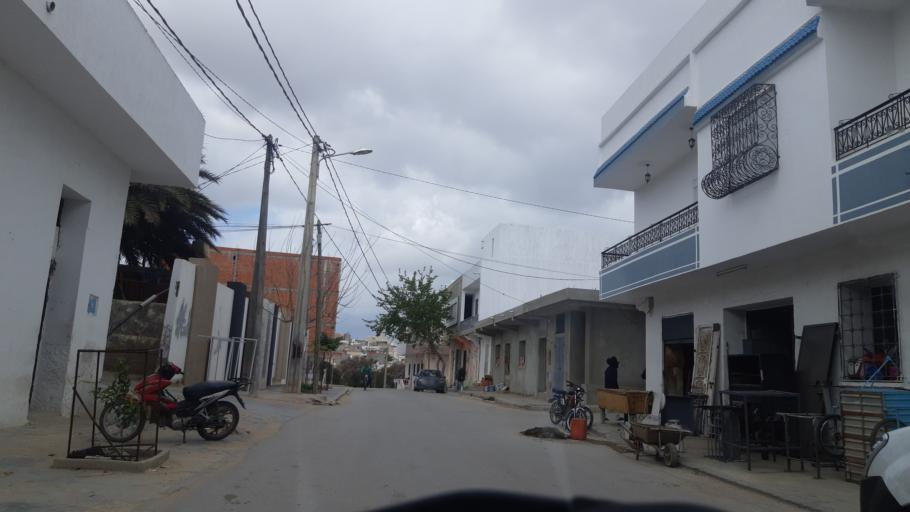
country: TN
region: Susah
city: Akouda
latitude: 35.8656
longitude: 10.5370
